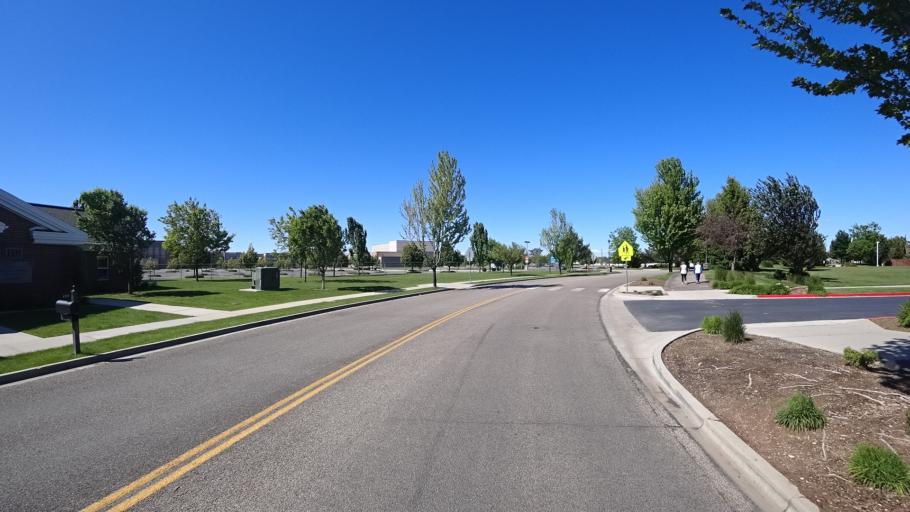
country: US
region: Idaho
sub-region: Ada County
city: Meridian
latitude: 43.6560
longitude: -116.4107
